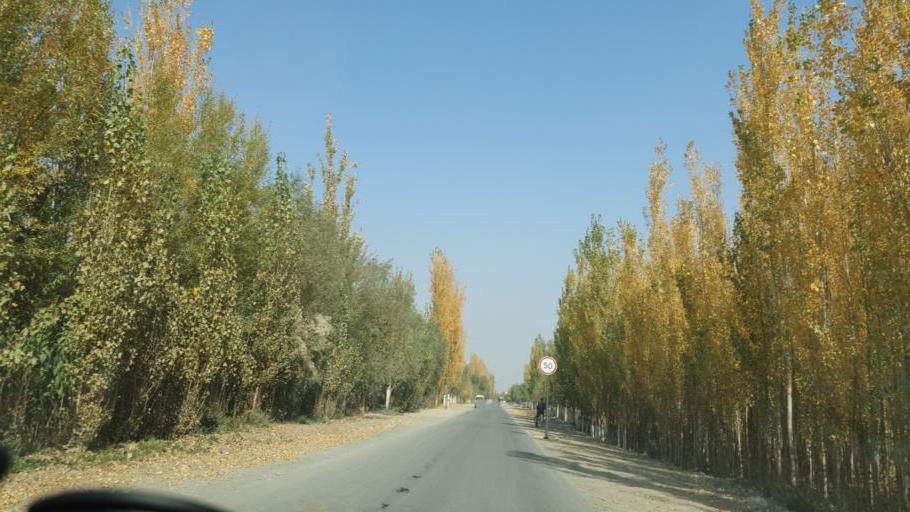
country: UZ
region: Fergana
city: Beshariq
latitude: 40.4888
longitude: 70.6203
